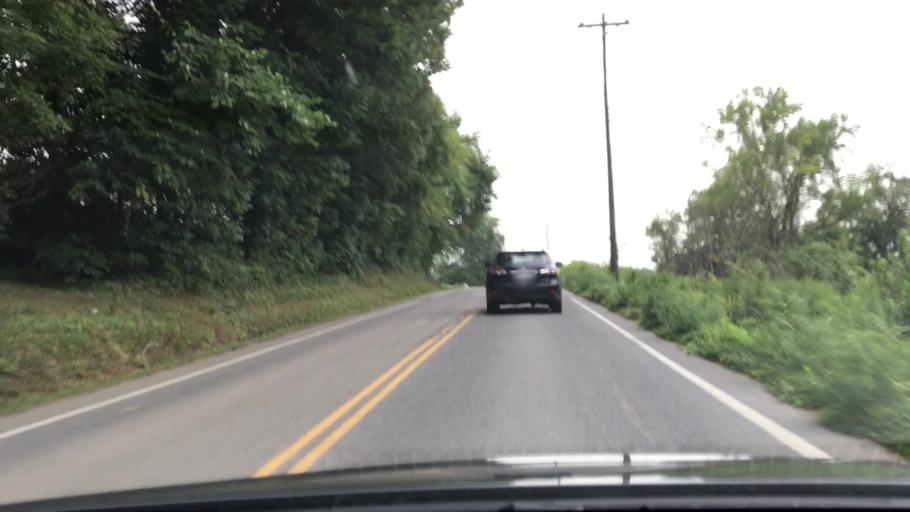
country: US
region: Tennessee
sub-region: Williamson County
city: Nolensville
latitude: 35.9368
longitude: -86.6962
